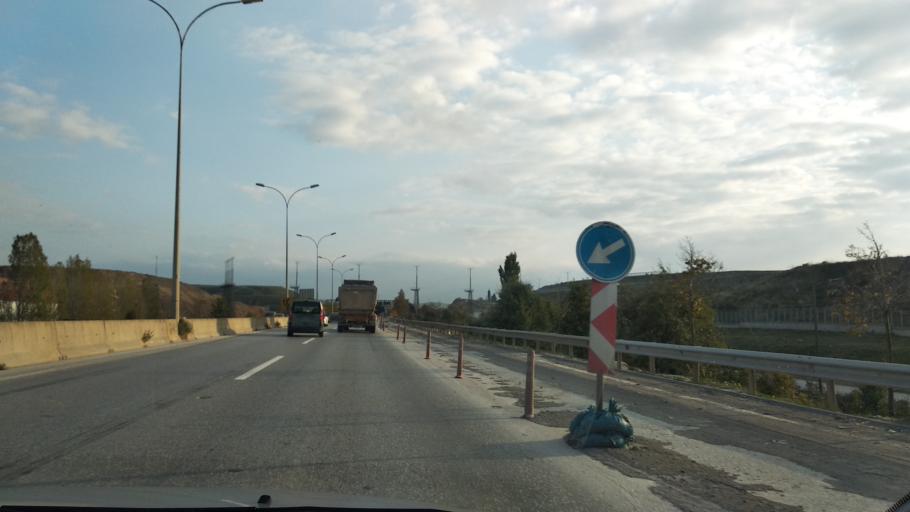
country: TR
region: Istanbul
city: Pendik
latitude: 40.9084
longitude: 29.3270
